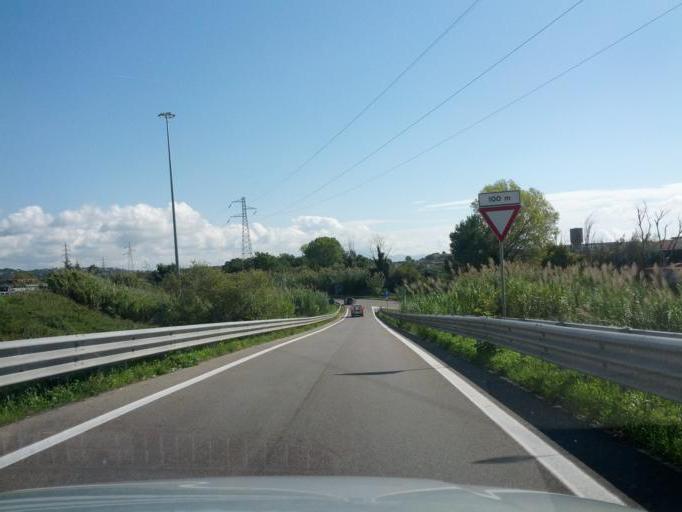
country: IT
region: Latium
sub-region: Provincia di Latina
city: Penitro
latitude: 41.2674
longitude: 13.6819
